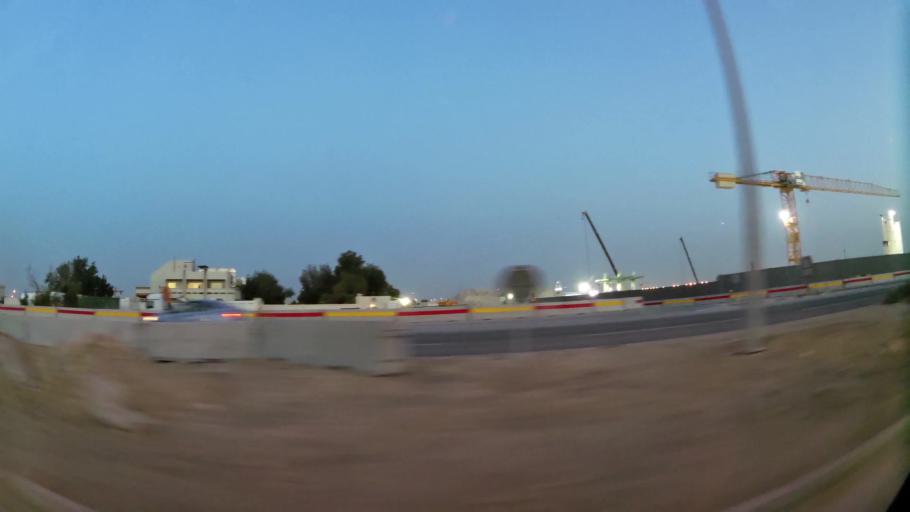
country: QA
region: Baladiyat ar Rayyan
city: Ar Rayyan
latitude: 25.3061
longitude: 51.4544
